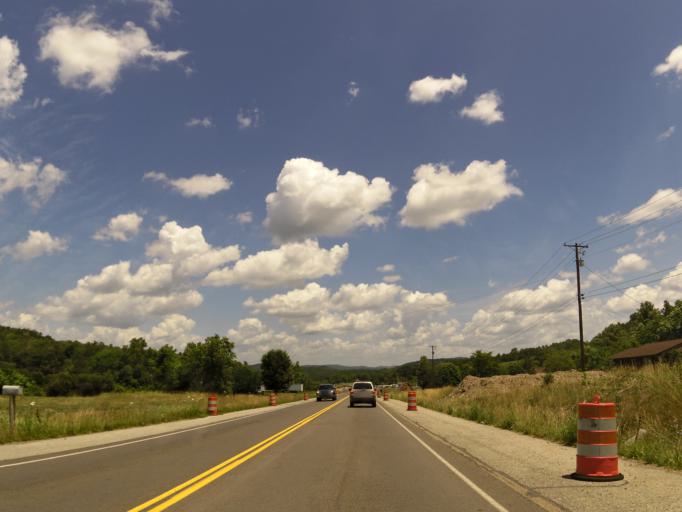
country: US
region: Tennessee
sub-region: Union County
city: Condon
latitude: 36.1634
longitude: -83.9104
